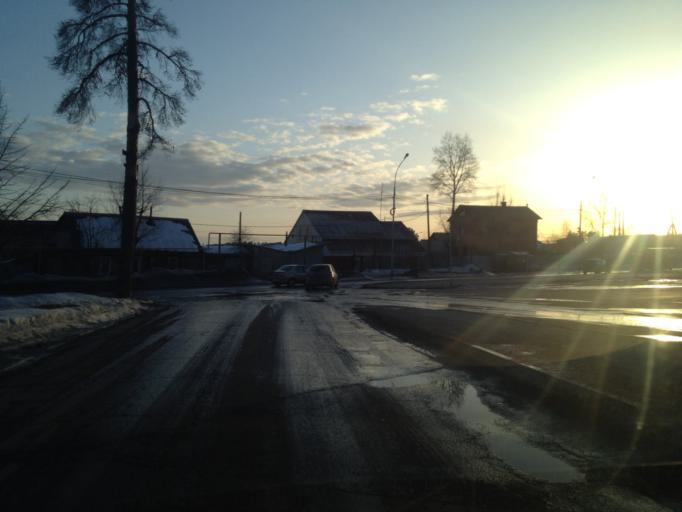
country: RU
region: Sverdlovsk
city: Sovkhoznyy
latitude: 56.7653
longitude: 60.5575
